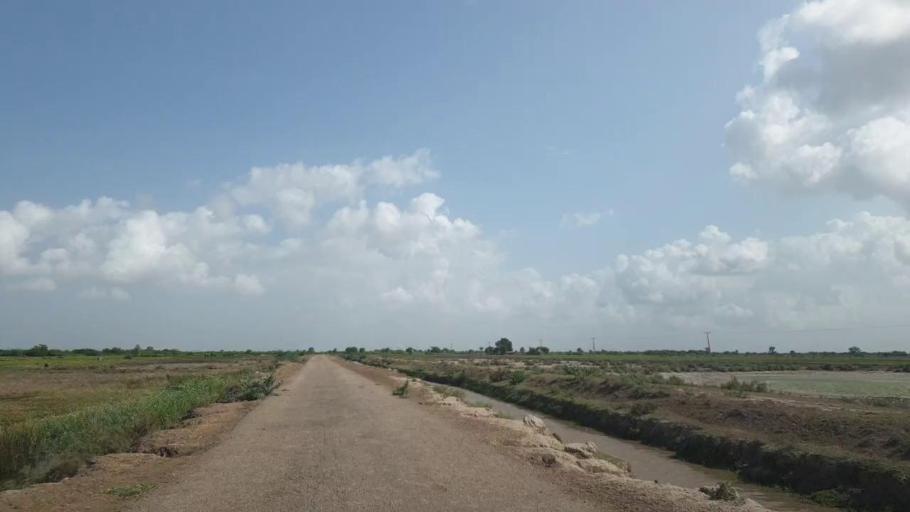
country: PK
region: Sindh
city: Kadhan
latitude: 24.5699
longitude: 69.0674
